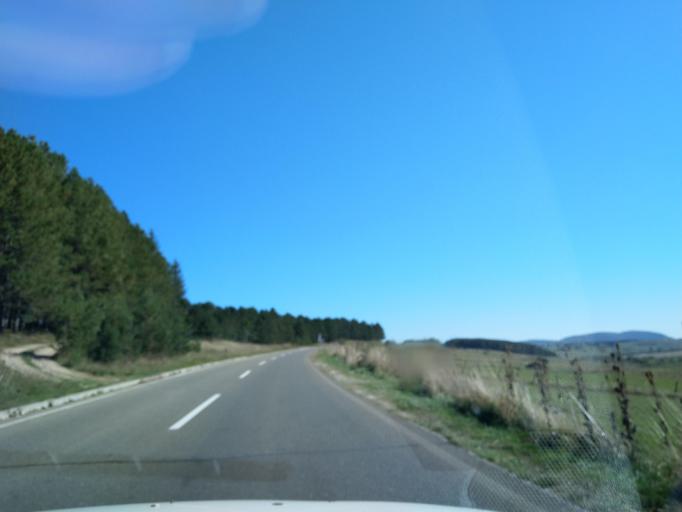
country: RS
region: Central Serbia
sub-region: Zlatiborski Okrug
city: Sjenica
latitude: 43.2679
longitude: 20.0332
